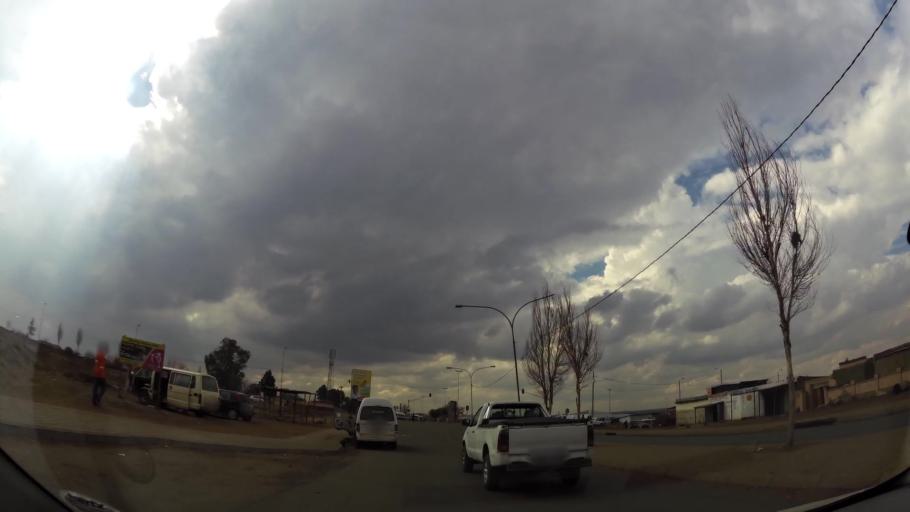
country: ZA
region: Gauteng
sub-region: Ekurhuleni Metropolitan Municipality
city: Germiston
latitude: -26.3909
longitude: 28.1608
